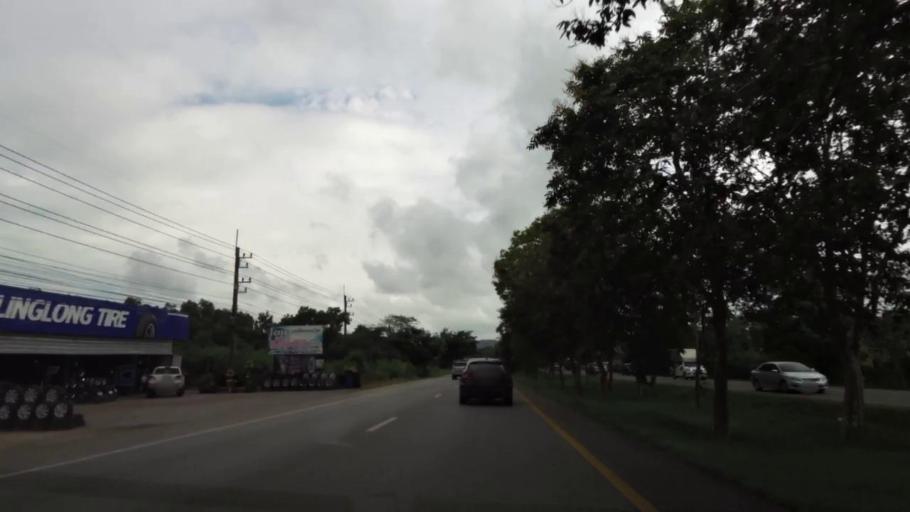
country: TH
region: Chanthaburi
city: Na Yai Am
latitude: 12.7295
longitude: 101.9195
